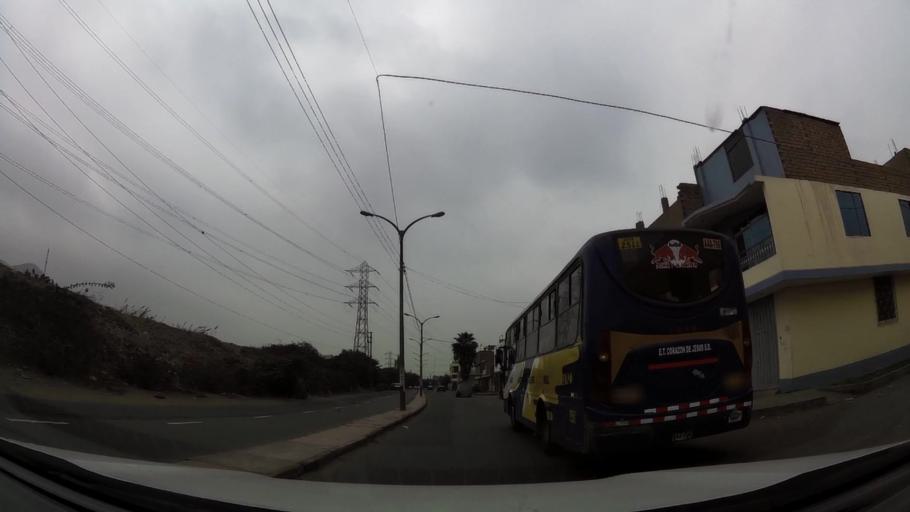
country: PE
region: Lima
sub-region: Lima
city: Independencia
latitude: -11.9400
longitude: -77.0860
